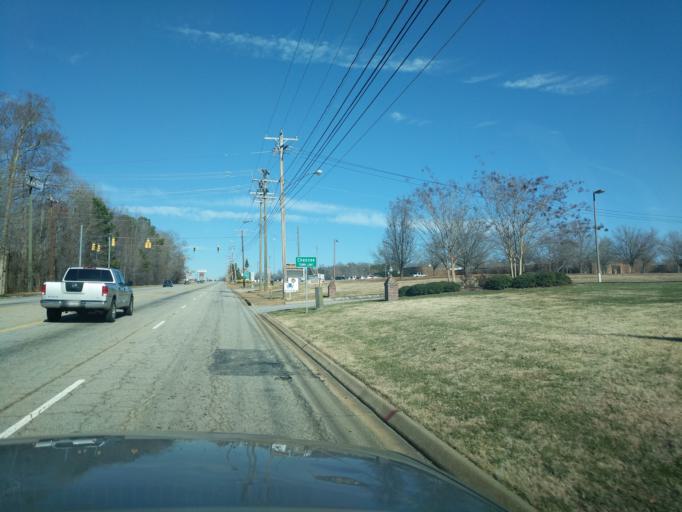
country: US
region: South Carolina
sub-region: Spartanburg County
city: Mayo
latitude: 35.1311
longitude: -81.8637
